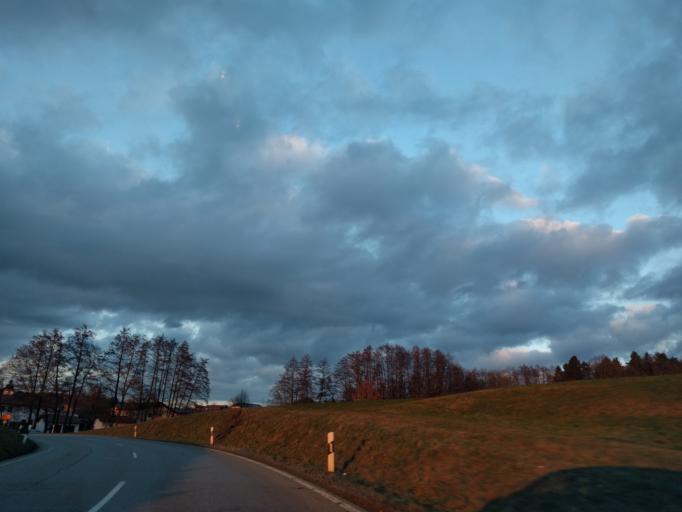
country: DE
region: Bavaria
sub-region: Lower Bavaria
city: Hofkirchen
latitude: 48.6904
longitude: 13.1213
